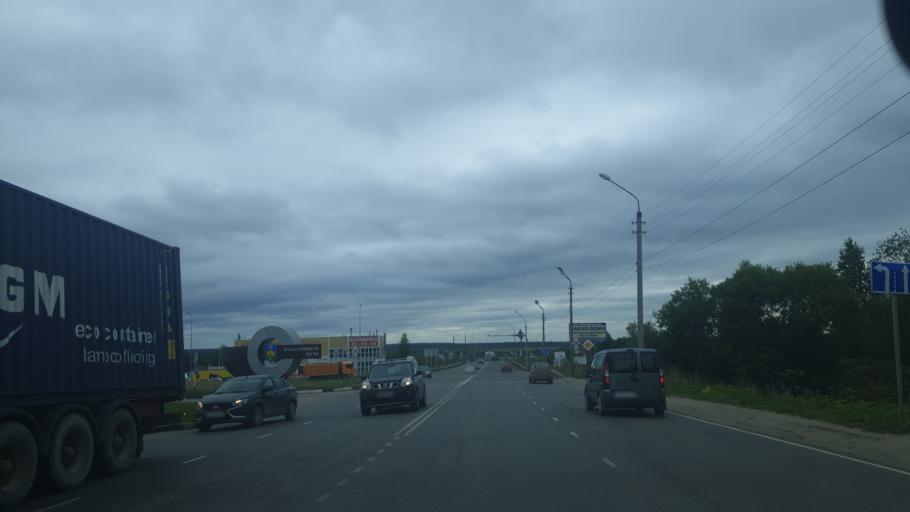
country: RU
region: Komi Republic
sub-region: Syktyvdinskiy Rayon
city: Syktyvkar
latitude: 61.6369
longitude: 50.8130
